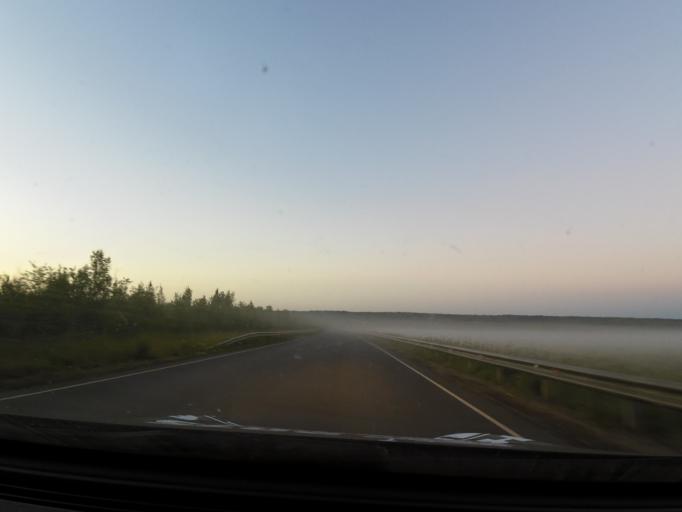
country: RU
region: Vologda
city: Vytegra
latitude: 60.9104
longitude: 36.0592
